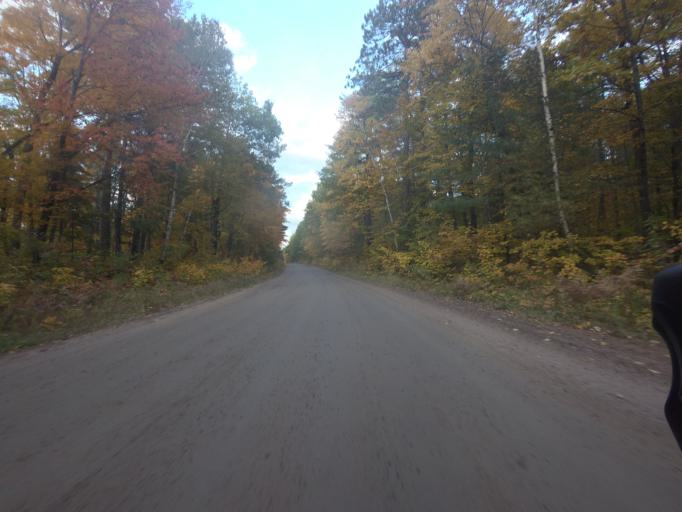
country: CA
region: Ontario
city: Deep River
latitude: 45.8938
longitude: -77.6176
